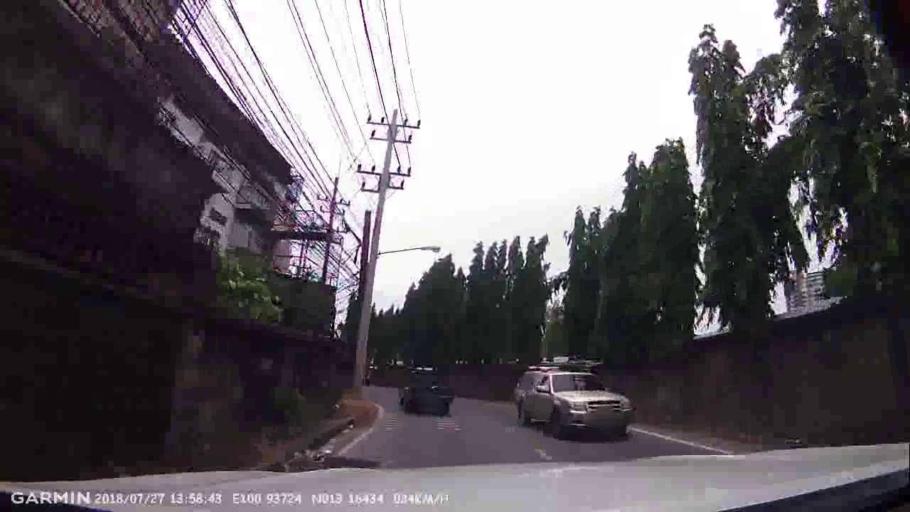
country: TH
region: Chon Buri
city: Si Racha
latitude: 13.1644
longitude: 100.9372
